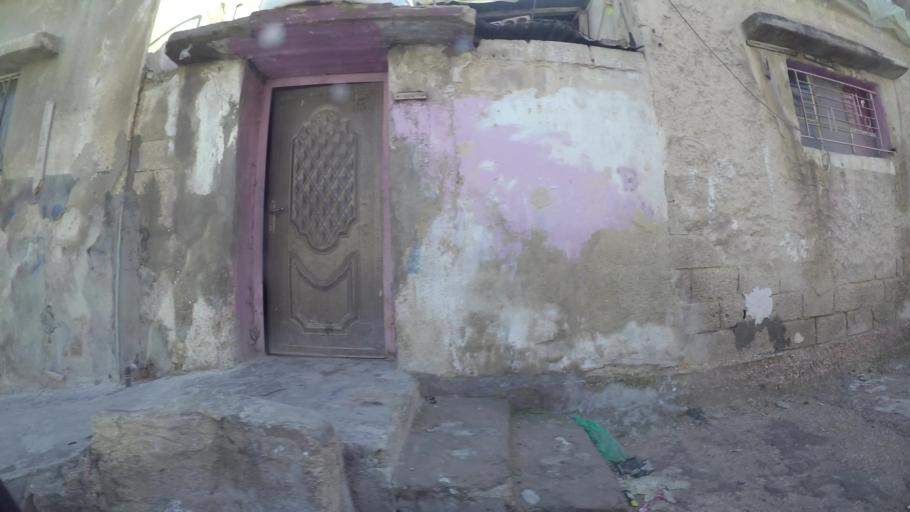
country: JO
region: Amman
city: Al Jubayhah
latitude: 32.0733
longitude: 35.8465
